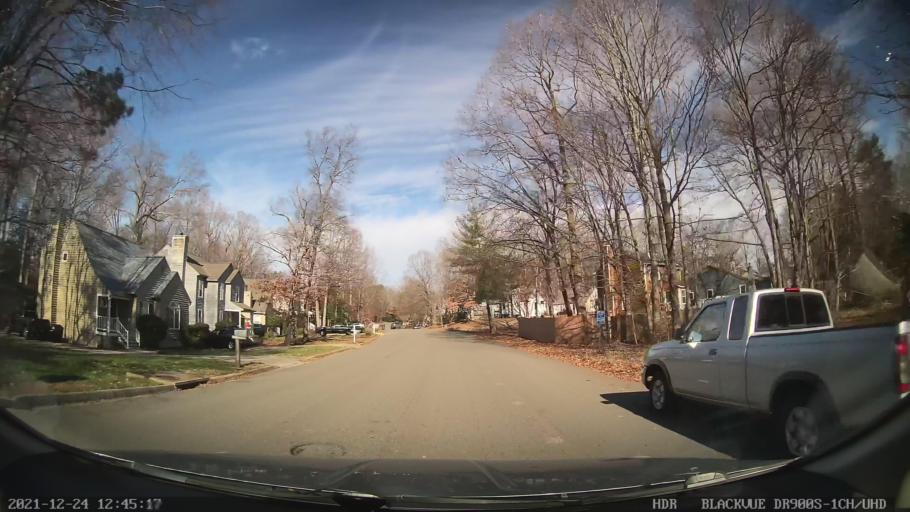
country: US
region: Virginia
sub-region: Henrico County
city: Short Pump
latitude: 37.6300
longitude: -77.6264
